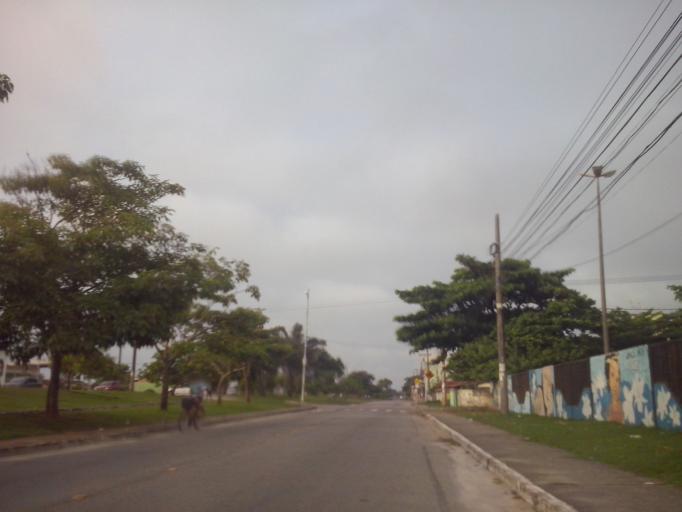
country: BR
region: Rio de Janeiro
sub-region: Rio Das Ostras
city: Rio das Ostras
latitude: -22.5515
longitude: -41.9764
